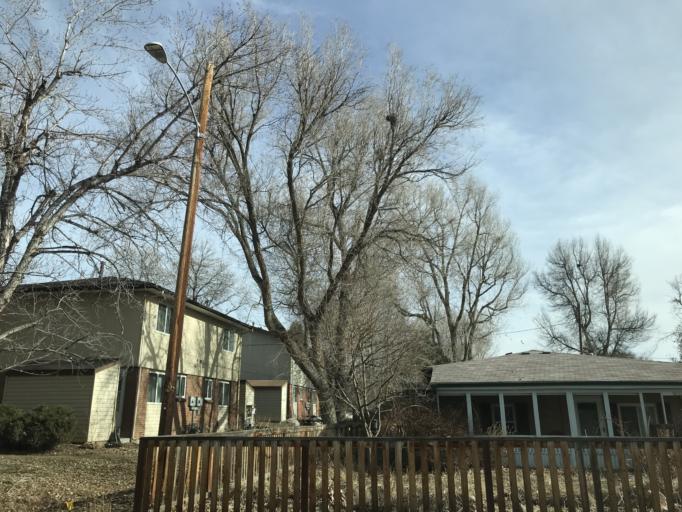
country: US
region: Colorado
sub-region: Arapahoe County
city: Littleton
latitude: 39.6060
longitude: -105.0116
